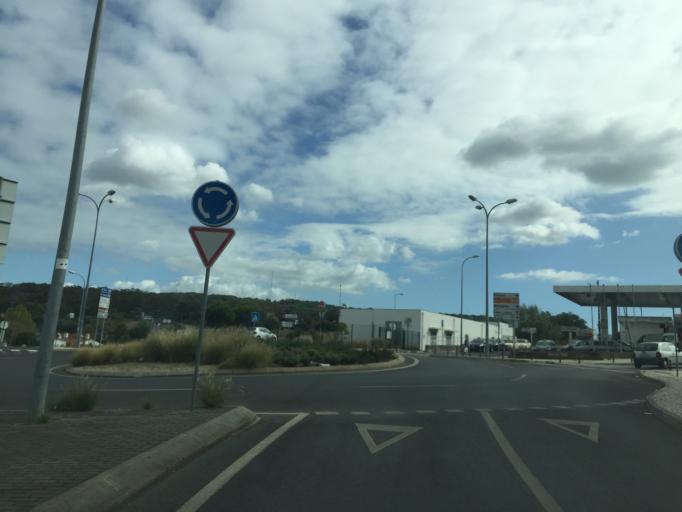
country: PT
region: Lisbon
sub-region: Odivelas
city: Pontinha
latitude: 38.7432
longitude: -9.2058
